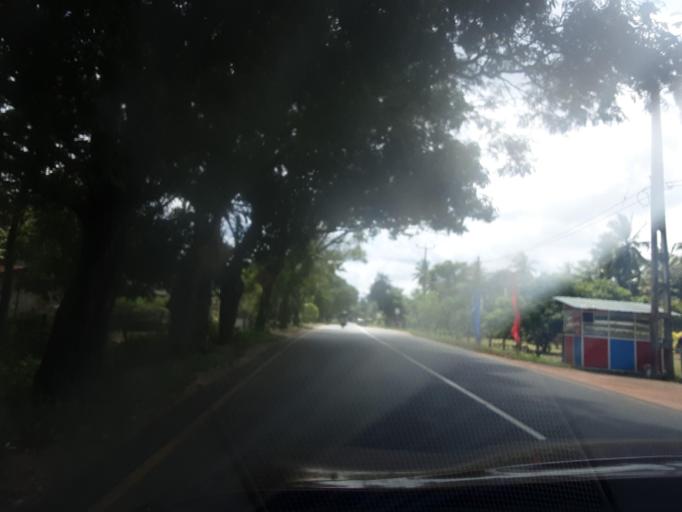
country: LK
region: North Western
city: Kuliyapitiya
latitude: 7.4767
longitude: 80.0071
